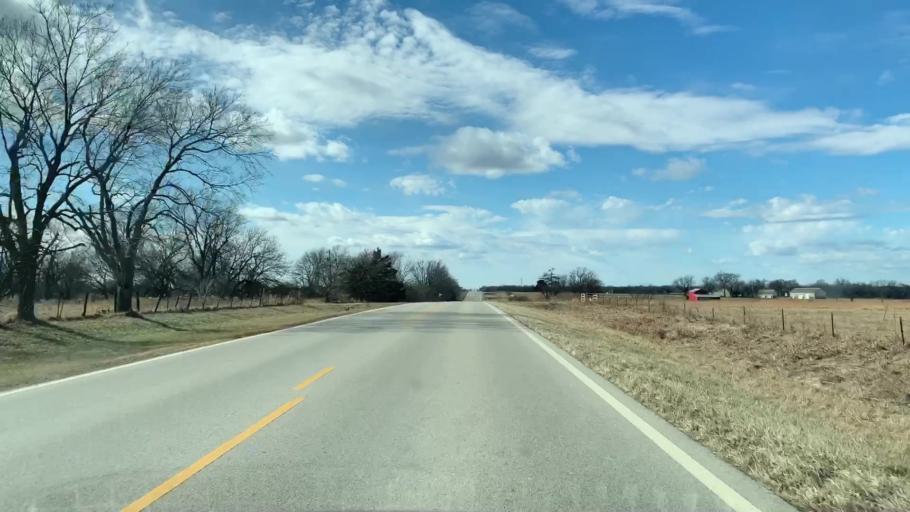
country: US
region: Kansas
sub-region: Neosho County
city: Chanute
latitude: 37.5287
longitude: -95.4445
